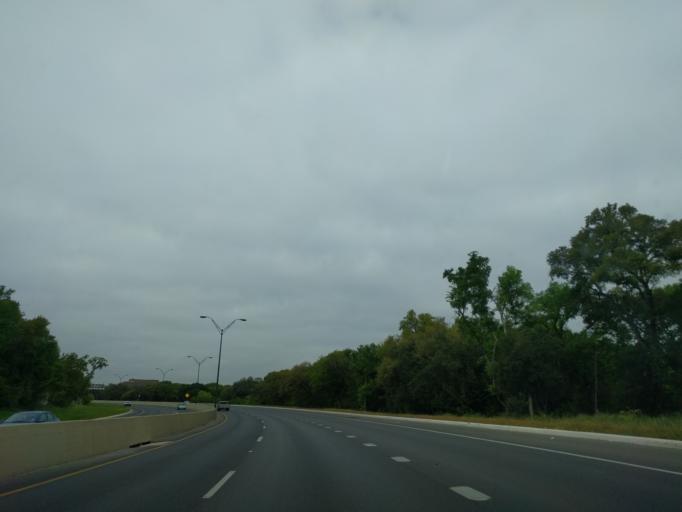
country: US
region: Texas
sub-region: Bexar County
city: Hollywood Park
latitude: 29.5531
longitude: -98.4779
